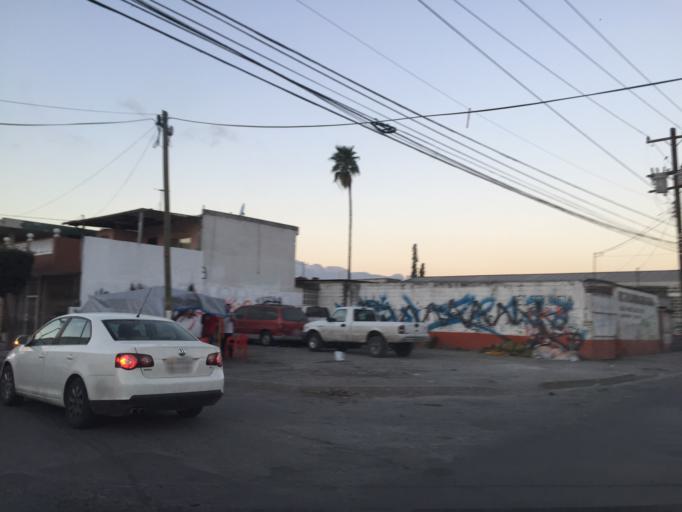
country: MX
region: Nuevo Leon
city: Guadalupe
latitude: 25.6953
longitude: -100.2290
